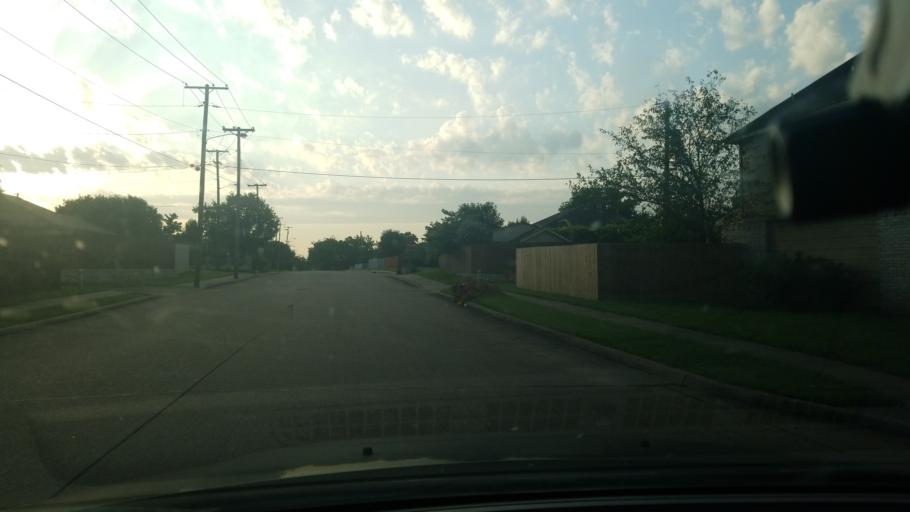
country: US
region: Texas
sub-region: Dallas County
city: Balch Springs
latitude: 32.7277
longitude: -96.6532
